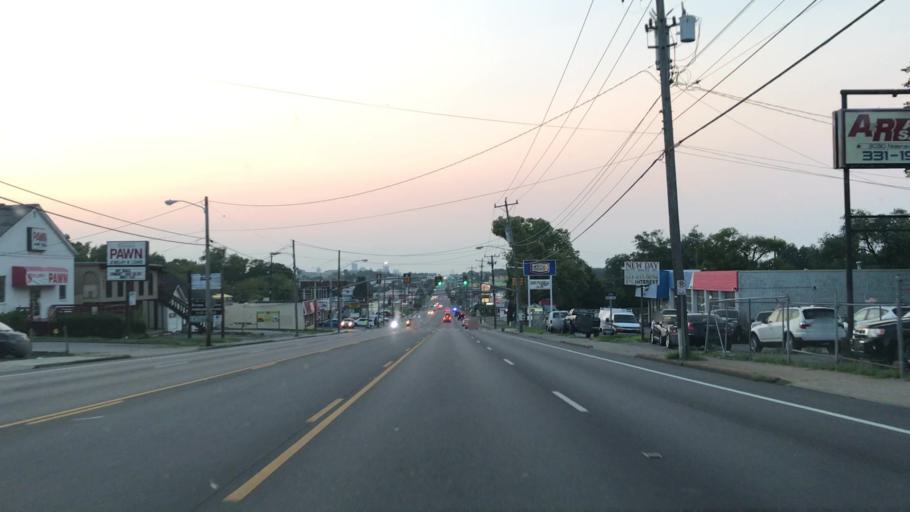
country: US
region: Tennessee
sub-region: Davidson County
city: Oak Hill
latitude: 36.1053
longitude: -86.7423
